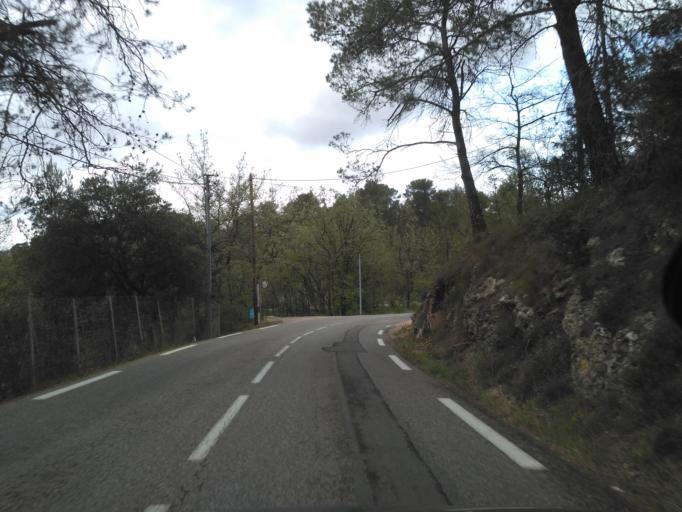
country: FR
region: Provence-Alpes-Cote d'Azur
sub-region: Departement du Var
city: Barjols
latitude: 43.6041
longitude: 5.9548
